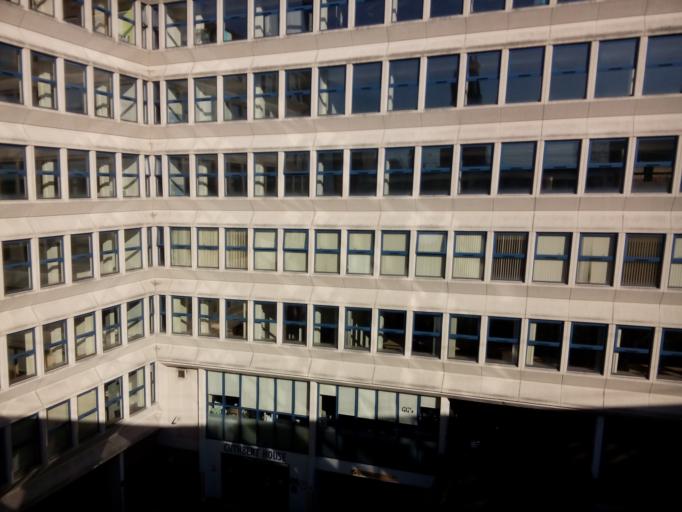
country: GB
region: England
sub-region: Newcastle upon Tyne
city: Newcastle upon Tyne
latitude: 54.9708
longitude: -1.6076
